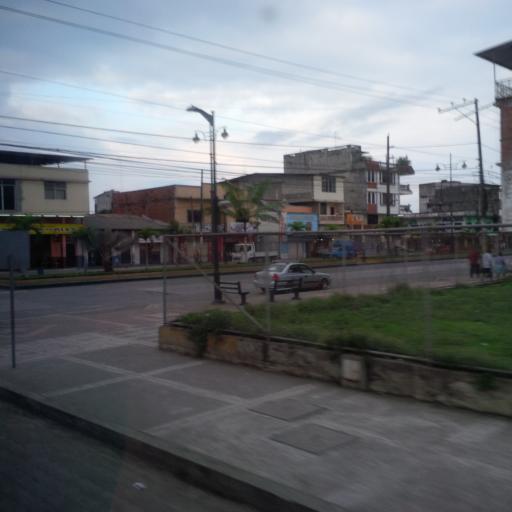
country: EC
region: Canar
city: La Troncal
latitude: -2.3298
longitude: -79.4058
